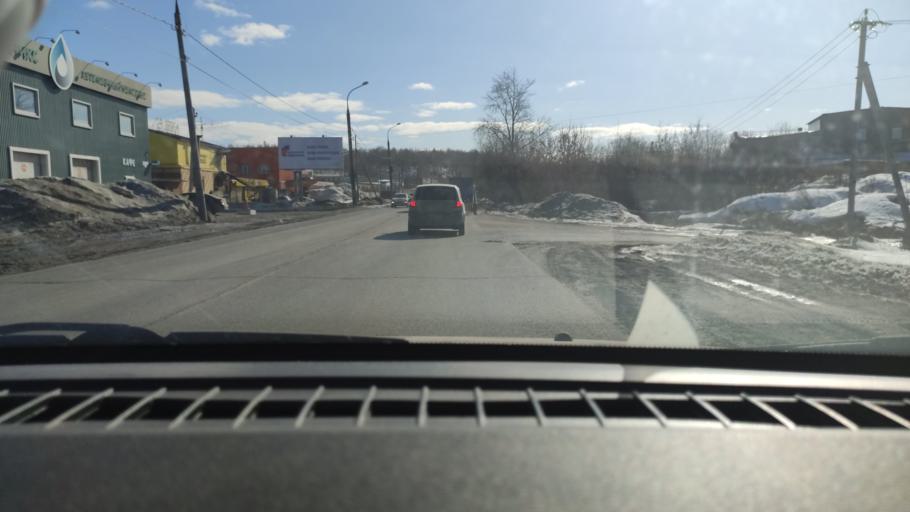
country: RU
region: Perm
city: Perm
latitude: 58.0752
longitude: 56.3495
